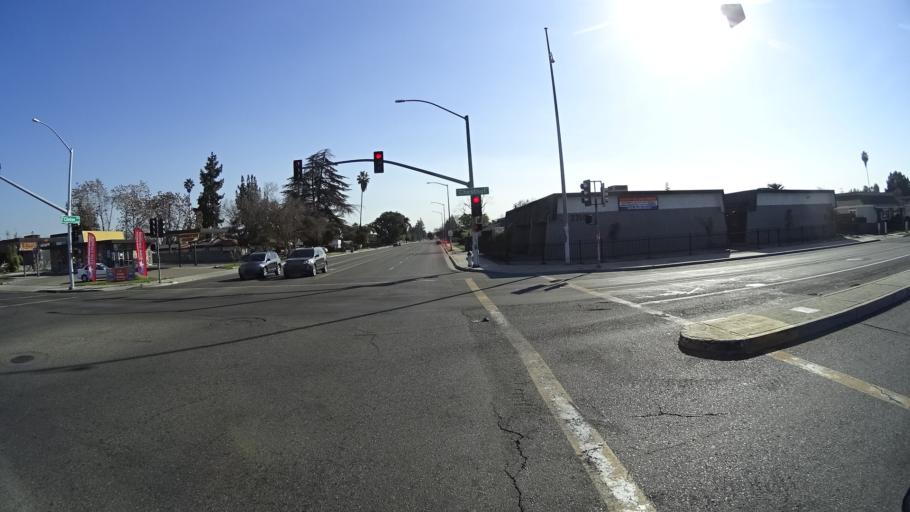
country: US
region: California
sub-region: Fresno County
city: Tarpey Village
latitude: 36.7722
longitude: -119.7365
